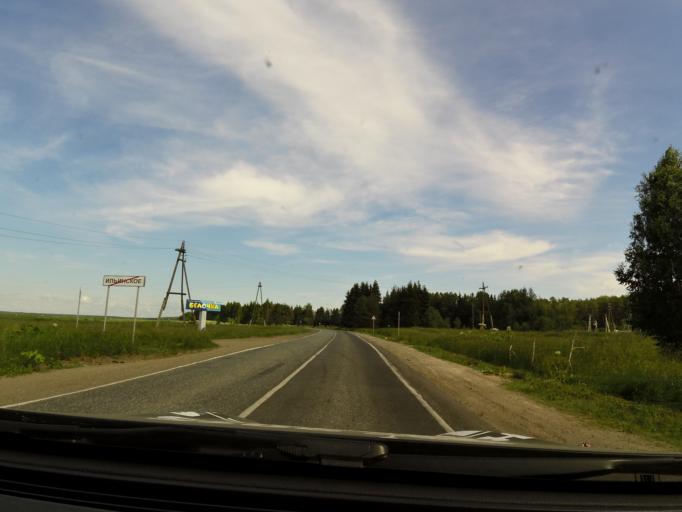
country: RU
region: Kirov
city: Slobodskoy
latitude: 58.7803
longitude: 50.4400
